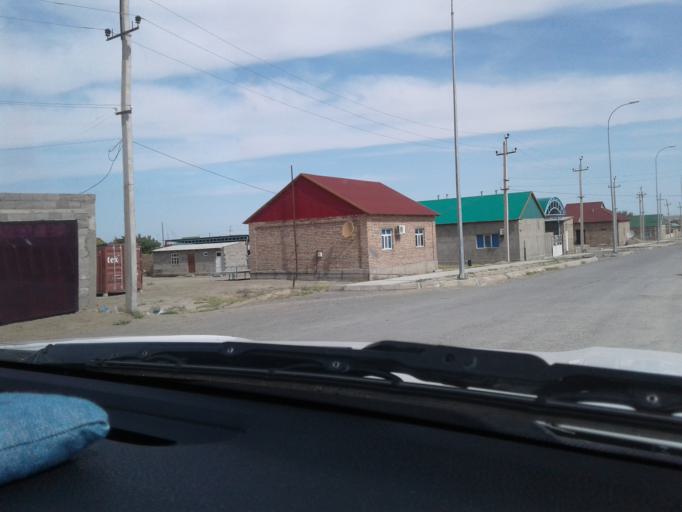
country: TM
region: Balkan
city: Gazanjyk
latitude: 39.2402
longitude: 55.5031
